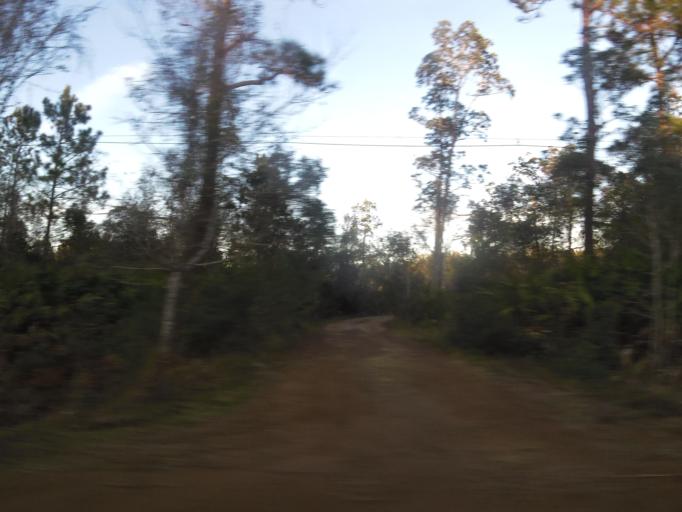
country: US
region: Florida
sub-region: Clay County
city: Green Cove Springs
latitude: 29.9006
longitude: -81.5835
